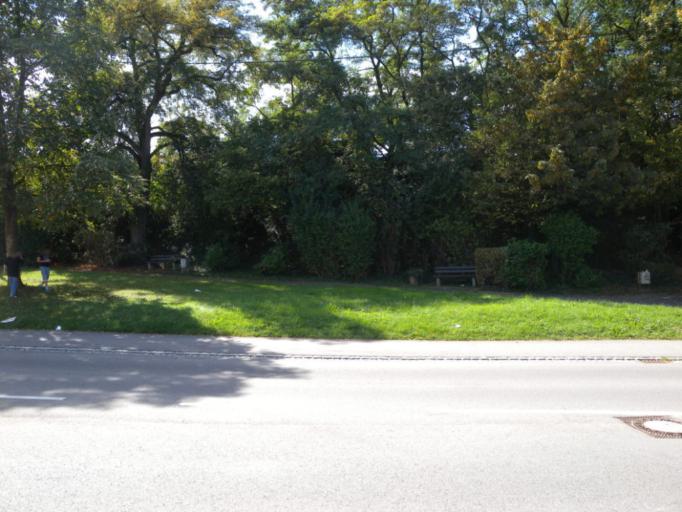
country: DE
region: Baden-Wuerttemberg
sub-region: Regierungsbezirk Stuttgart
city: Sersheim
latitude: 48.9579
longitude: 9.0177
